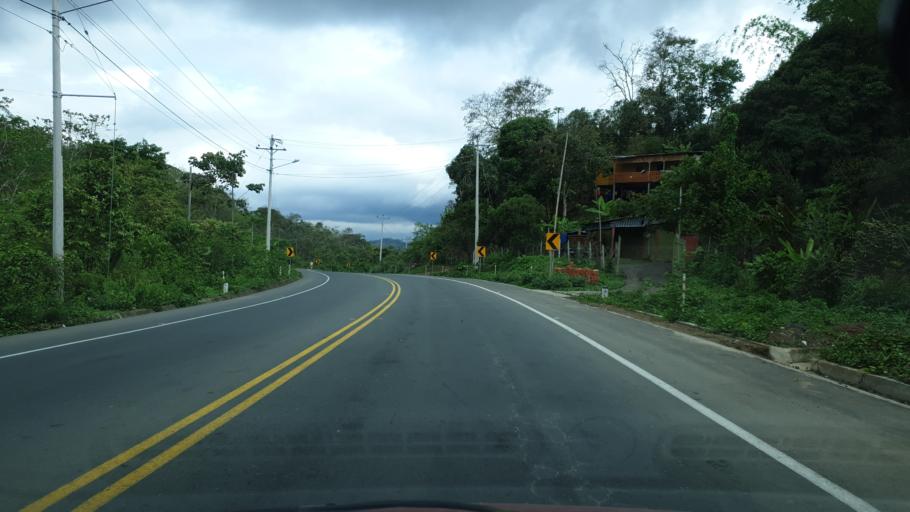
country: EC
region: Manabi
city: Pajan
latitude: -1.5621
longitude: -80.5240
